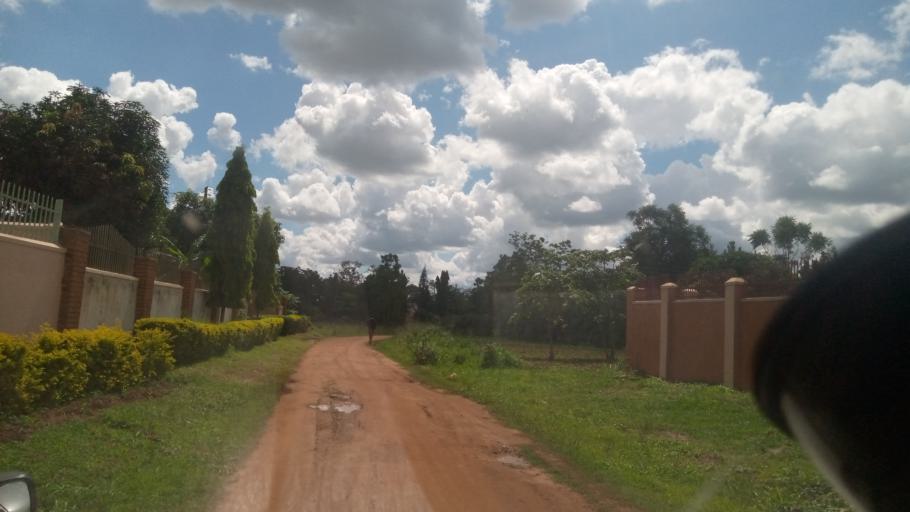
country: UG
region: Northern Region
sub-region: Lira District
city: Lira
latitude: 2.2426
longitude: 32.9050
